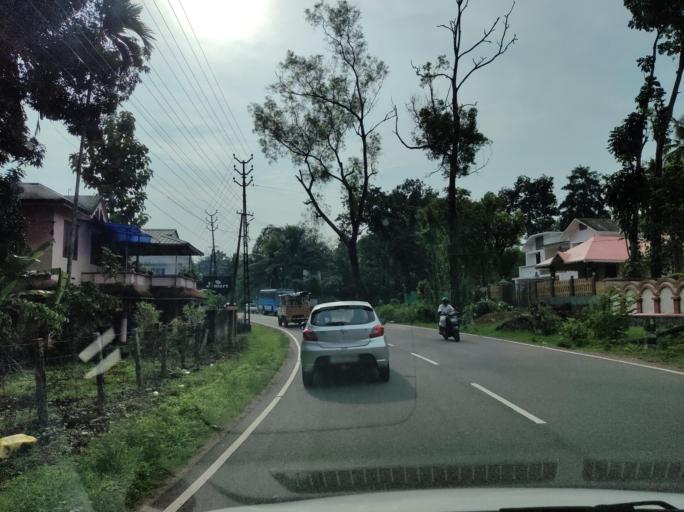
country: IN
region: Kerala
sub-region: Alappuzha
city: Kattanam
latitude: 9.1741
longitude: 76.5796
